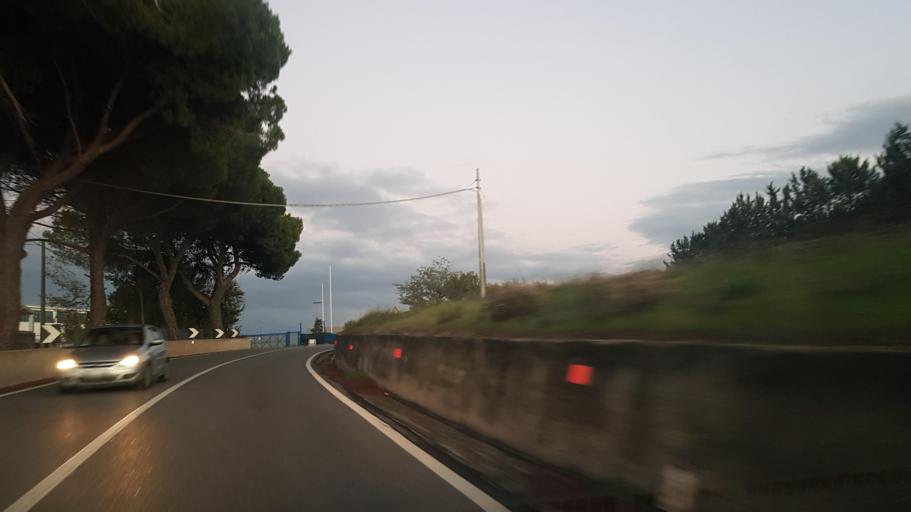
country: IT
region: Basilicate
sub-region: Provincia di Matera
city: Matera
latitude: 40.6782
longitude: 16.6564
